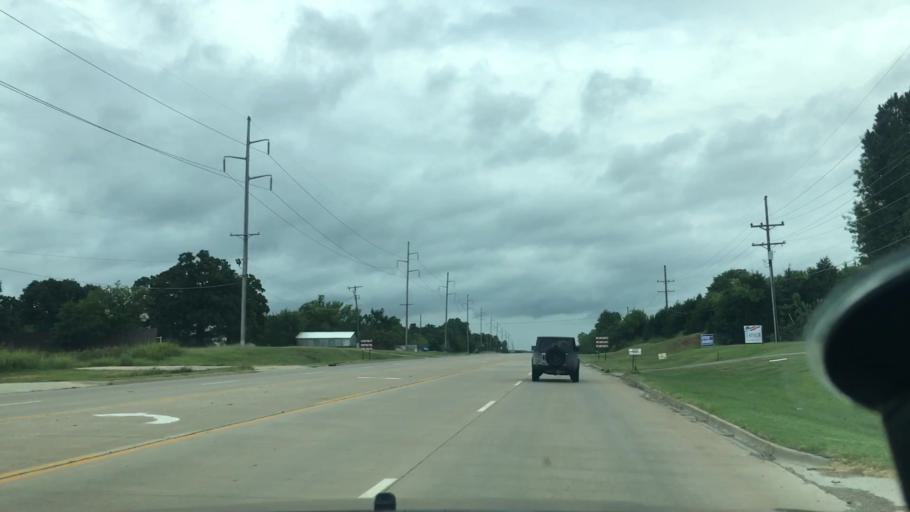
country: US
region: Oklahoma
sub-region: Seminole County
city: Seminole
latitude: 35.2574
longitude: -96.6712
